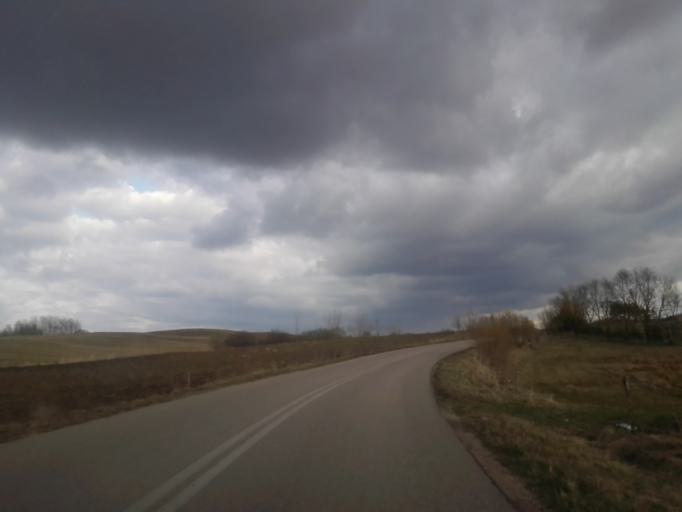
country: PL
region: Podlasie
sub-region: Suwalki
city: Suwalki
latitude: 54.2005
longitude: 22.9710
